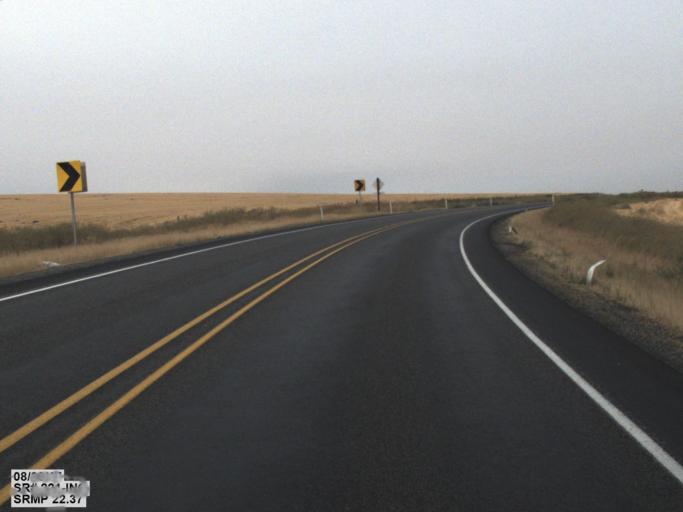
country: US
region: Washington
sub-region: Benton County
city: Prosser
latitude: 46.1897
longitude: -119.7057
